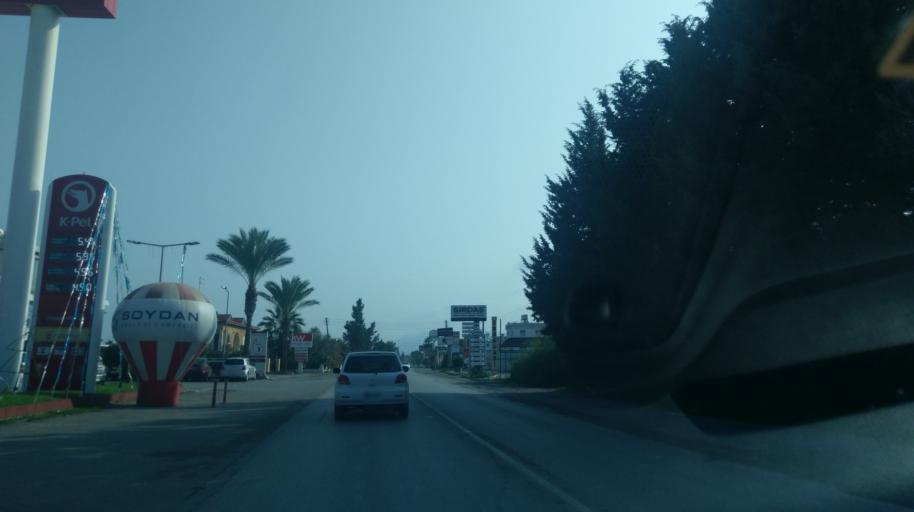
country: CY
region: Keryneia
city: Kyrenia
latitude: 35.3304
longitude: 33.3473
